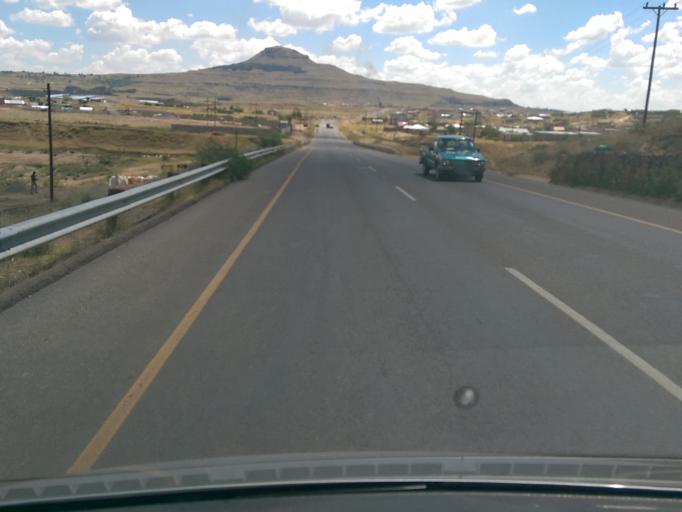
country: LS
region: Maseru
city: Maseru
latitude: -29.3765
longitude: 27.4934
